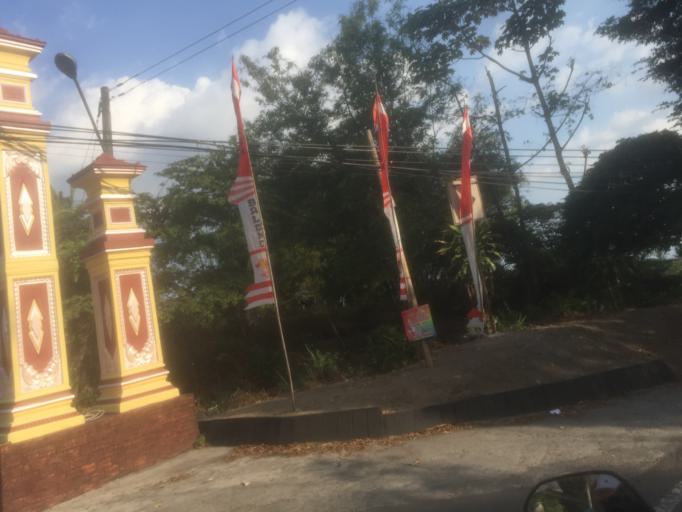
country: ID
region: Daerah Istimewa Yogyakarta
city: Sleman
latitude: -7.6554
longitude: 110.4238
